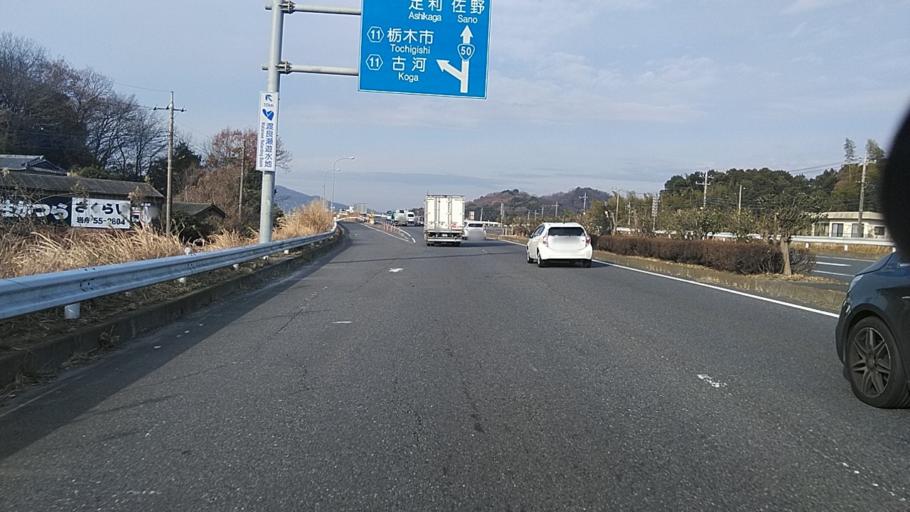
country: JP
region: Tochigi
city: Fujioka
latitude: 36.3131
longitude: 139.6771
